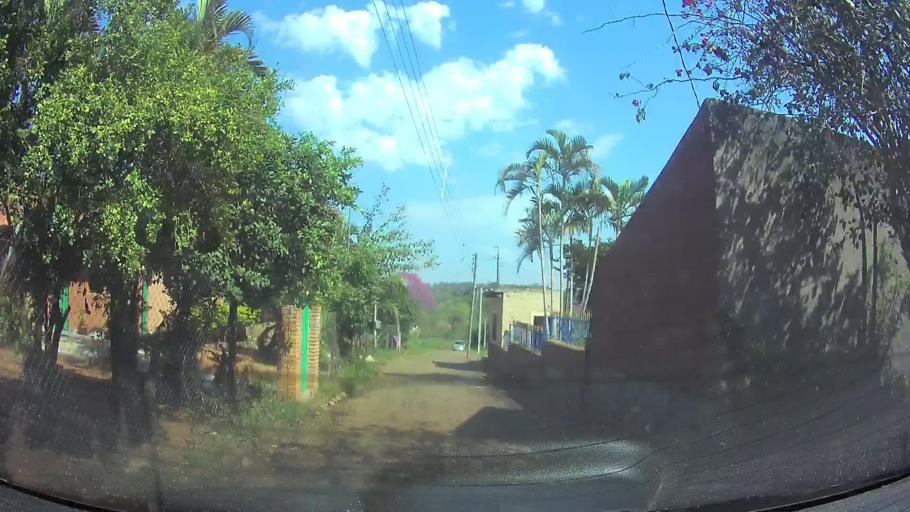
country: PY
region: Central
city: Limpio
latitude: -25.2333
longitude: -57.4410
